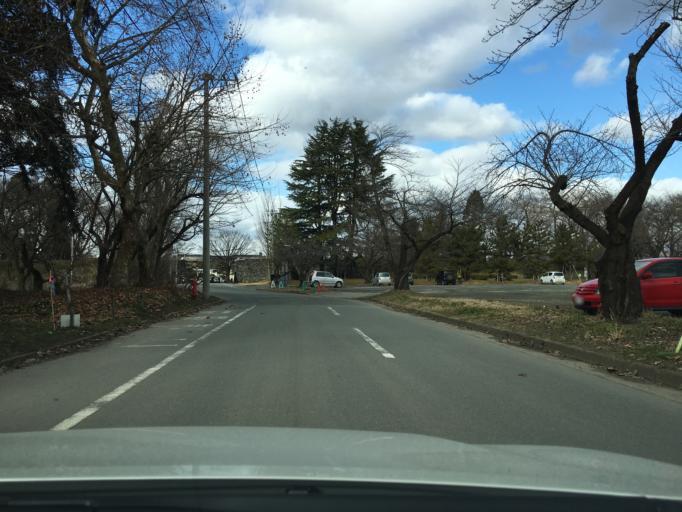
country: JP
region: Yamagata
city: Yamagata-shi
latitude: 38.2568
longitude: 140.3274
